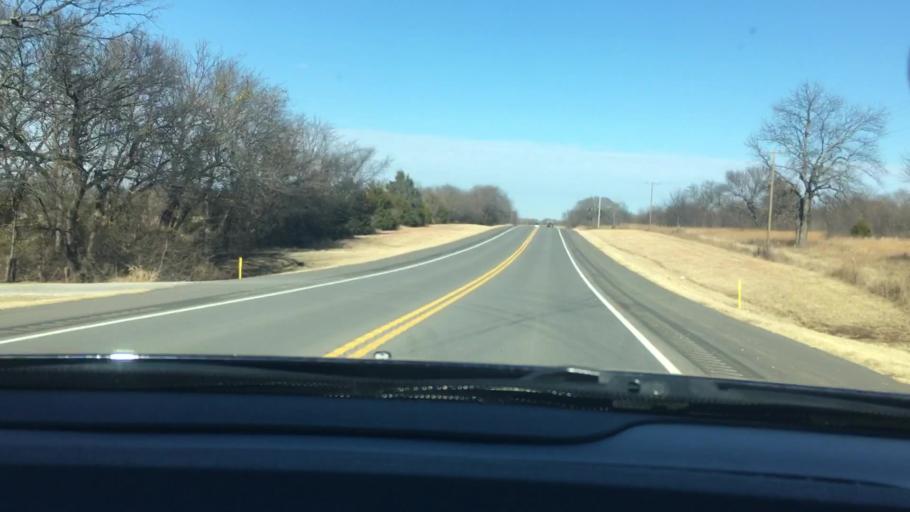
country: US
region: Oklahoma
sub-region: Murray County
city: Davis
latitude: 34.5579
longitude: -97.1339
